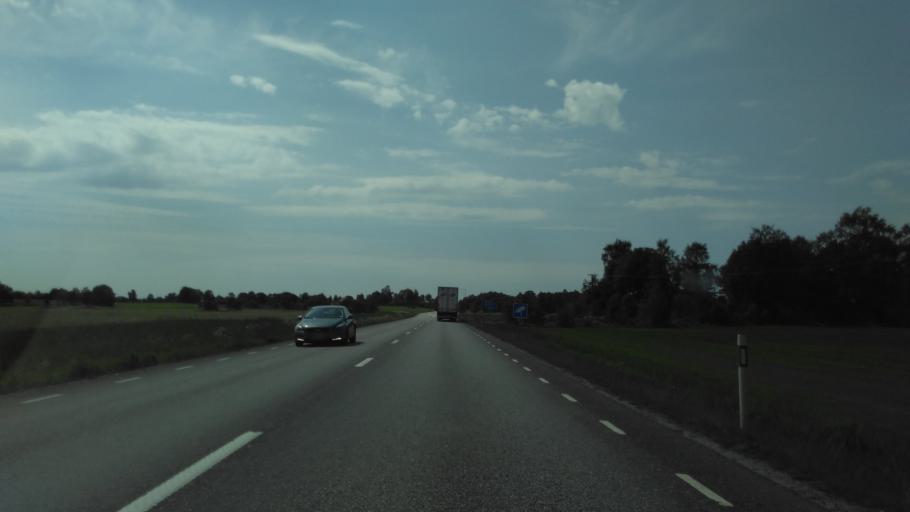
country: SE
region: Vaestra Goetaland
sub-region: Grastorps Kommun
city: Graestorp
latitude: 58.4057
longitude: 12.8274
